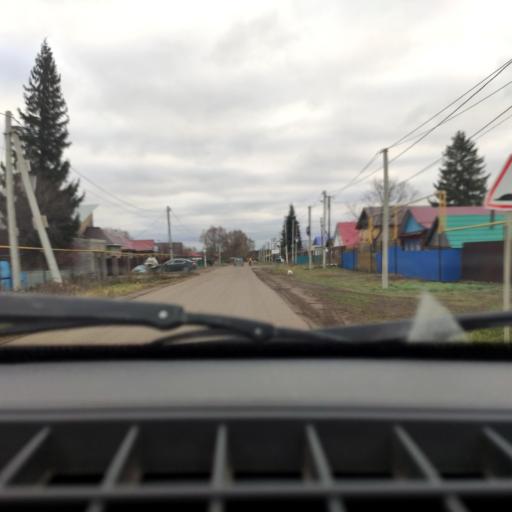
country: RU
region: Bashkortostan
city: Avdon
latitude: 54.6497
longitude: 55.7728
